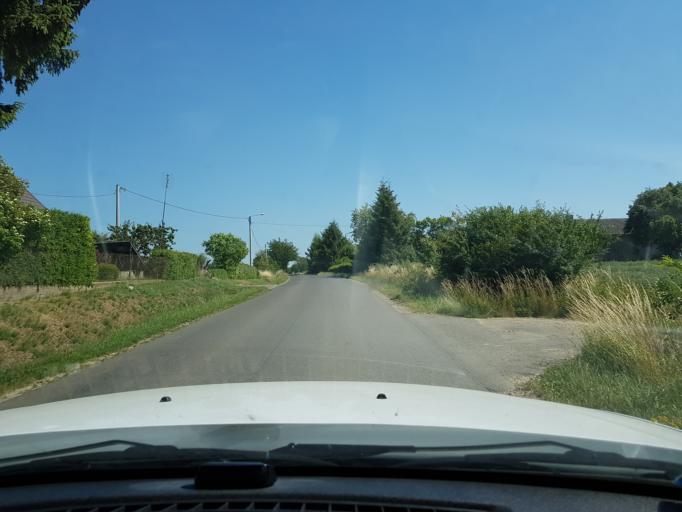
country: PL
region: West Pomeranian Voivodeship
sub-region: Powiat koszalinski
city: Mielno
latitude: 54.1911
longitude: 16.0578
